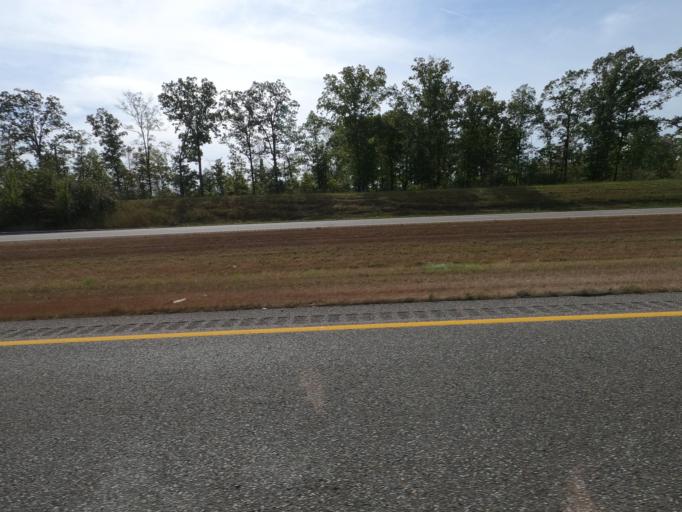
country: US
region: Tennessee
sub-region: Humphreys County
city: New Johnsonville
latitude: 35.8705
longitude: -88.0119
